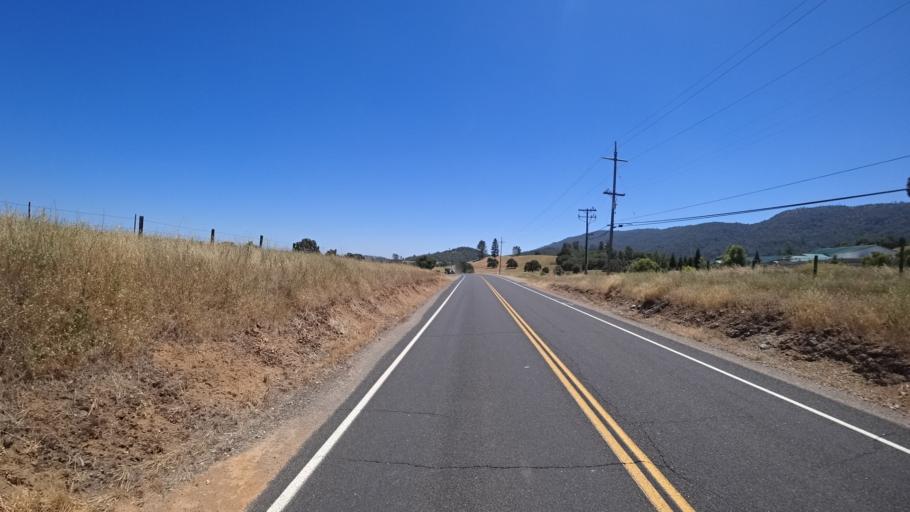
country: US
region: California
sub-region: Calaveras County
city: San Andreas
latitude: 38.1903
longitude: -120.6907
